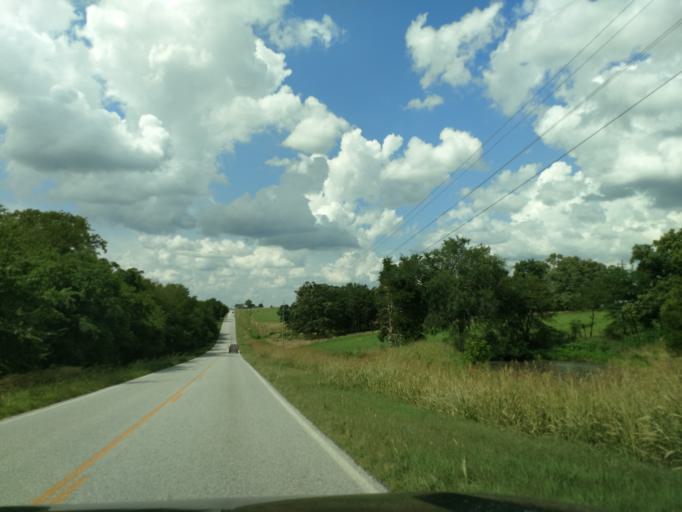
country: US
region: Arkansas
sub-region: Carroll County
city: Berryville
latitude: 36.4616
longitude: -93.5558
